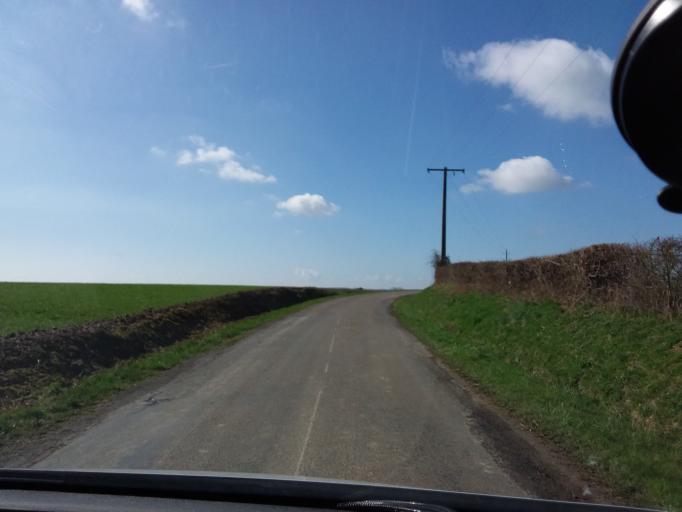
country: FR
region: Picardie
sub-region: Departement de l'Aisne
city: Origny-en-Thierache
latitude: 49.8160
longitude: 4.0297
